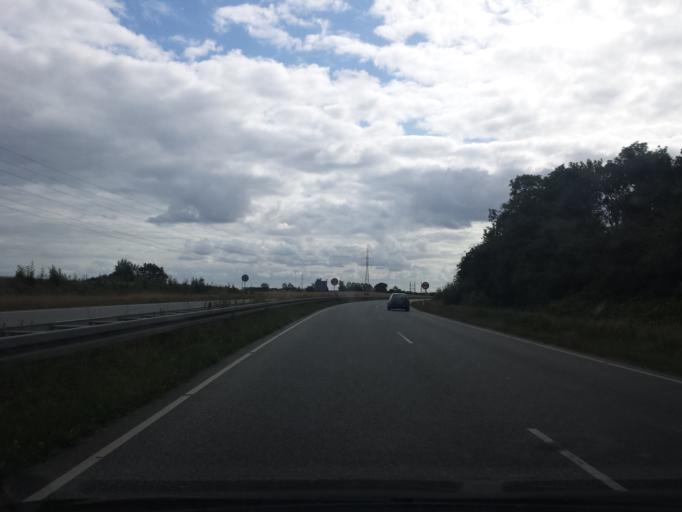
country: DK
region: South Denmark
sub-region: Sonderborg Kommune
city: Augustenborg
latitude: 54.9387
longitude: 9.8760
